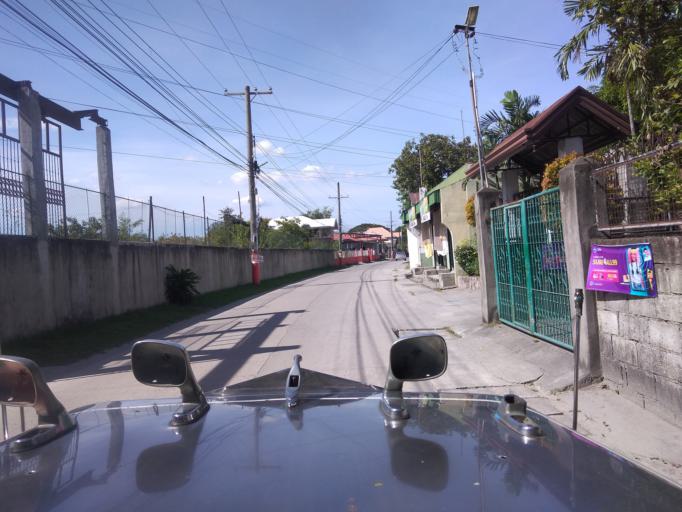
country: PH
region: Central Luzon
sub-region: Province of Pampanga
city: Magliman
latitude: 15.0285
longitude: 120.6682
